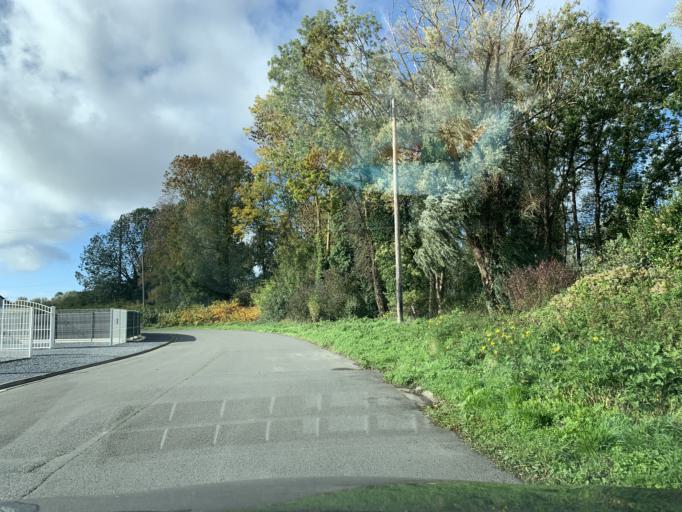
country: FR
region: Nord-Pas-de-Calais
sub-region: Departement du Nord
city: Neuville-Saint-Remy
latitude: 50.1895
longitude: 3.2370
